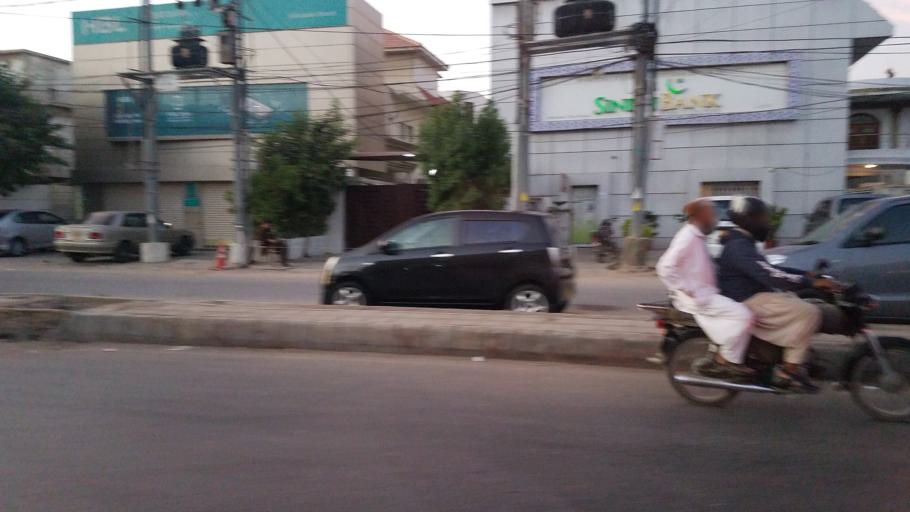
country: PK
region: Sindh
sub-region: Karachi District
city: Karachi
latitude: 24.8274
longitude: 67.0306
